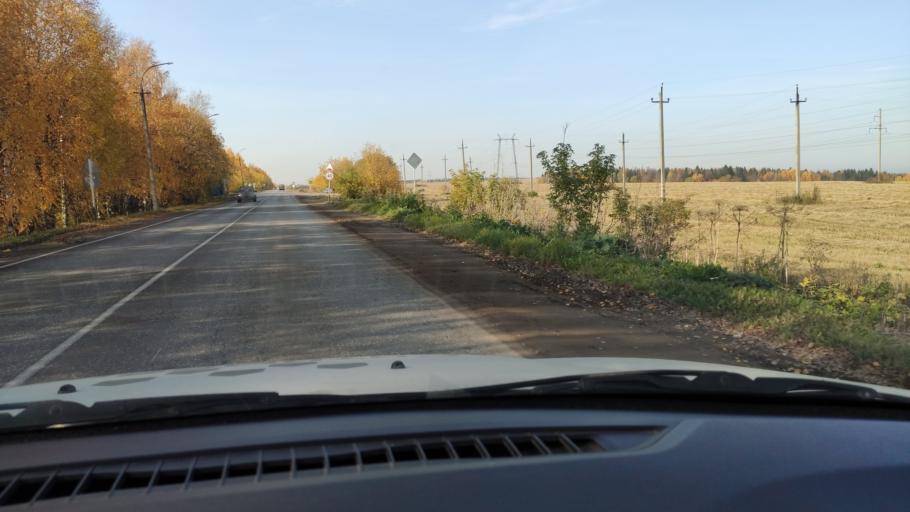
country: RU
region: Perm
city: Sylva
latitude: 58.0283
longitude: 56.7126
